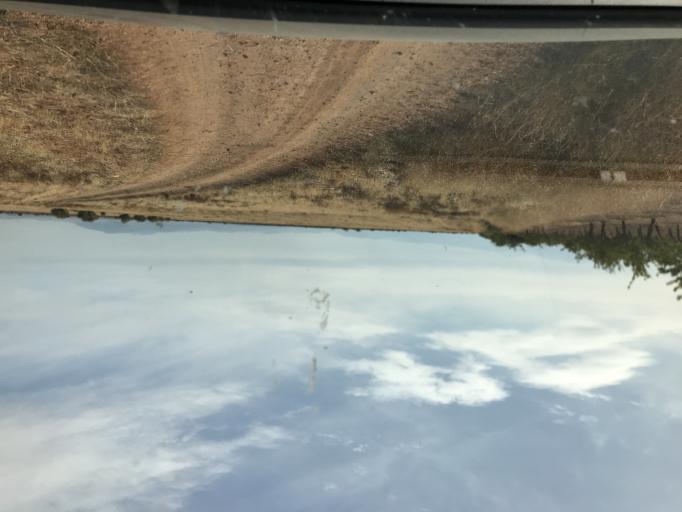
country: ES
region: Andalusia
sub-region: Provincia de Granada
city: Villanueva de las Torres
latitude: 37.4728
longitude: -3.0566
